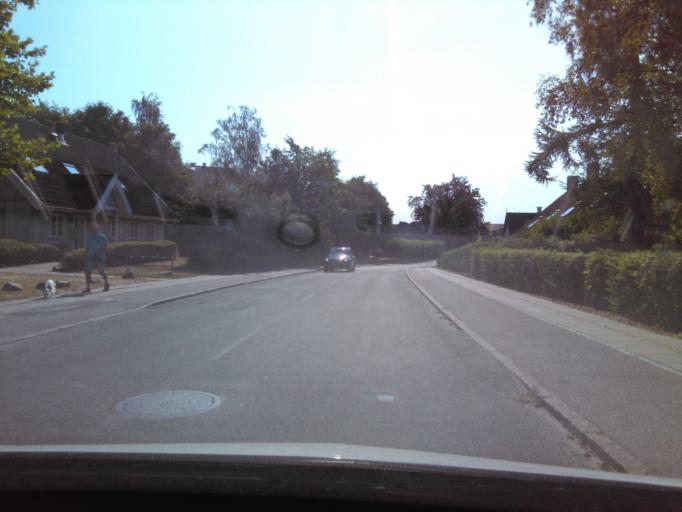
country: DK
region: Capital Region
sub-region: Fureso Kommune
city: Farum
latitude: 55.8146
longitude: 12.3700
